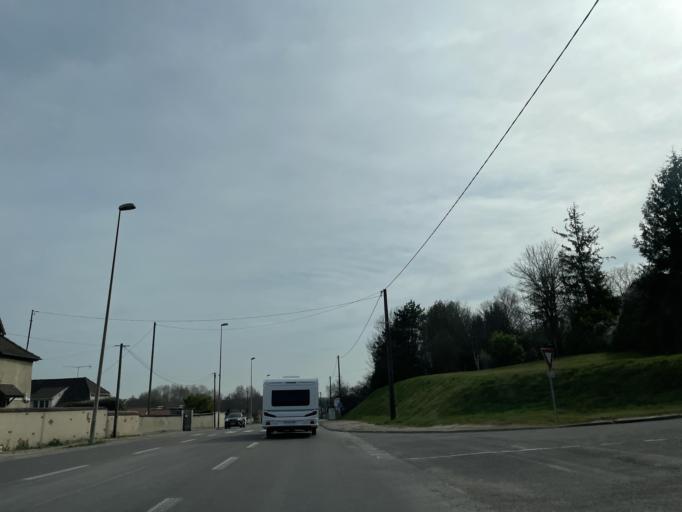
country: FR
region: Champagne-Ardenne
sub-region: Departement de l'Aube
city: Romilly-sur-Seine
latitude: 48.5159
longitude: 3.6541
